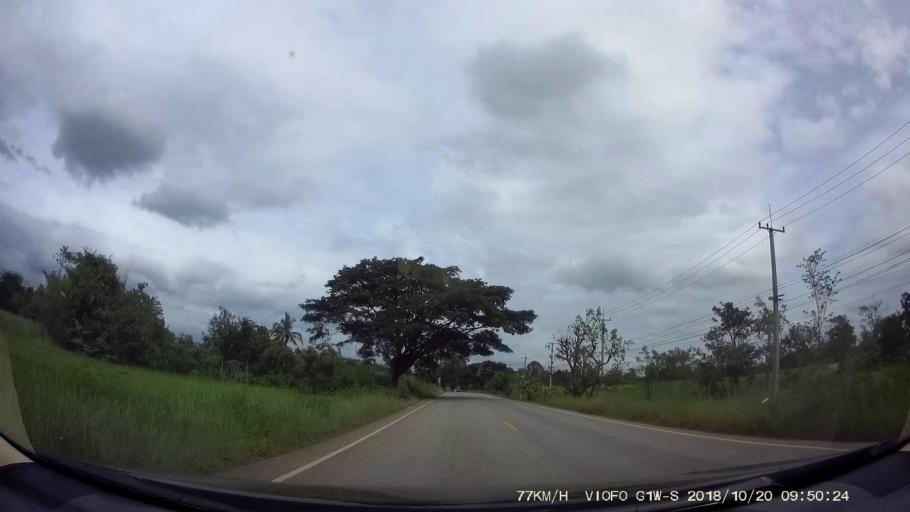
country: TH
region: Chaiyaphum
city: Khon San
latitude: 16.5307
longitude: 101.9023
